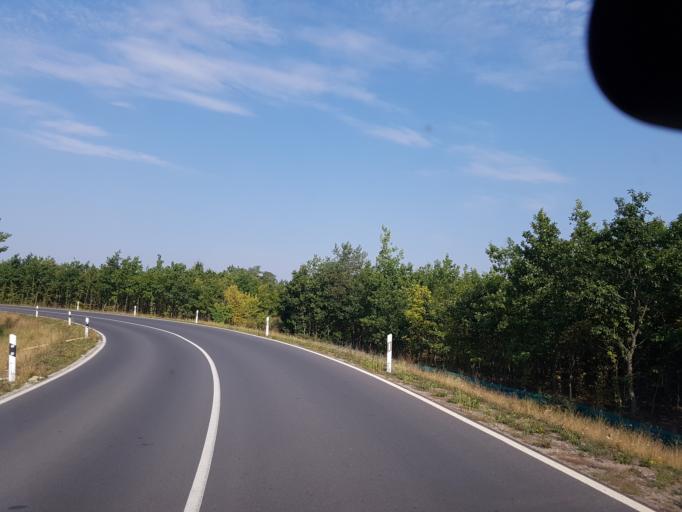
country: DE
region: Brandenburg
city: Lauchhammer
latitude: 51.5358
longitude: 13.7719
